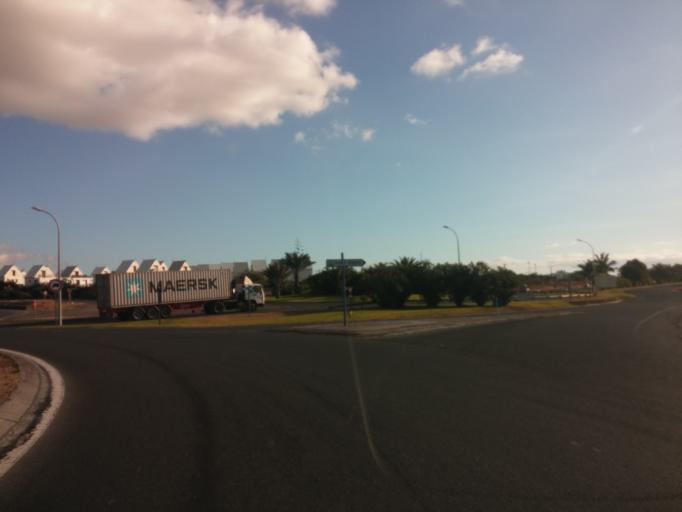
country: RE
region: Reunion
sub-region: Reunion
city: Le Port
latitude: -20.9300
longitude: 55.3092
